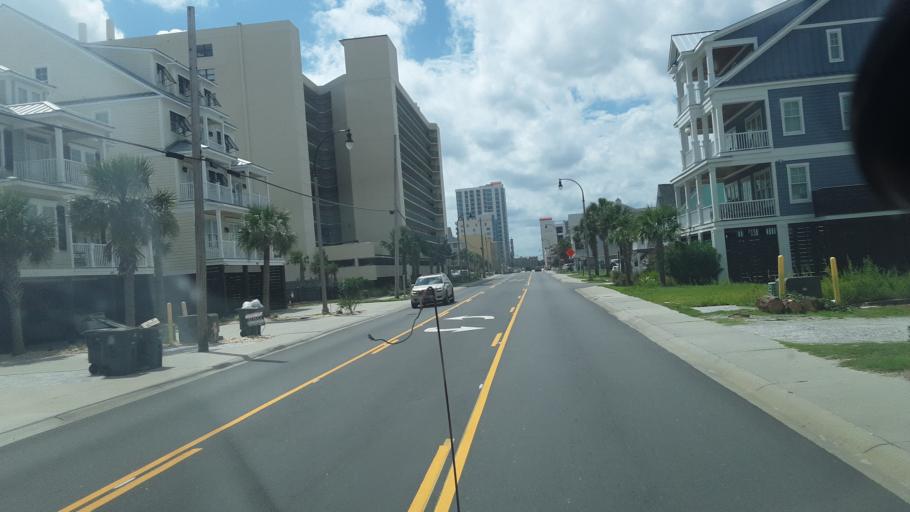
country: US
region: South Carolina
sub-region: Horry County
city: North Myrtle Beach
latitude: 33.8287
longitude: -78.6399
